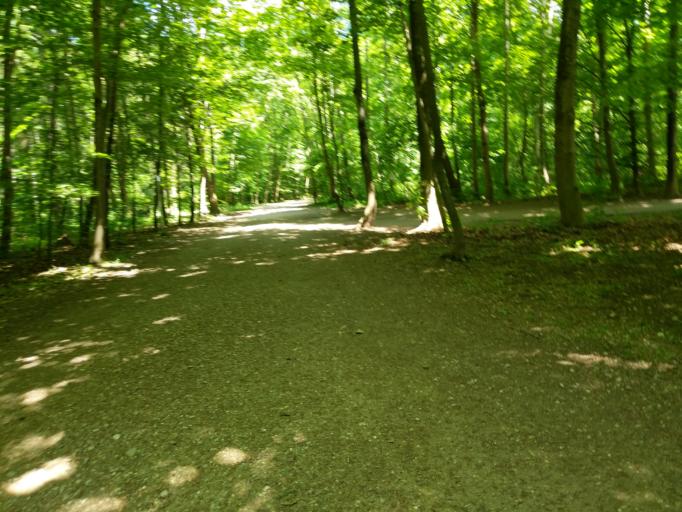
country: DE
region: Bavaria
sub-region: Upper Bavaria
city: Pullach im Isartal
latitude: 48.1029
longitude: 11.5086
